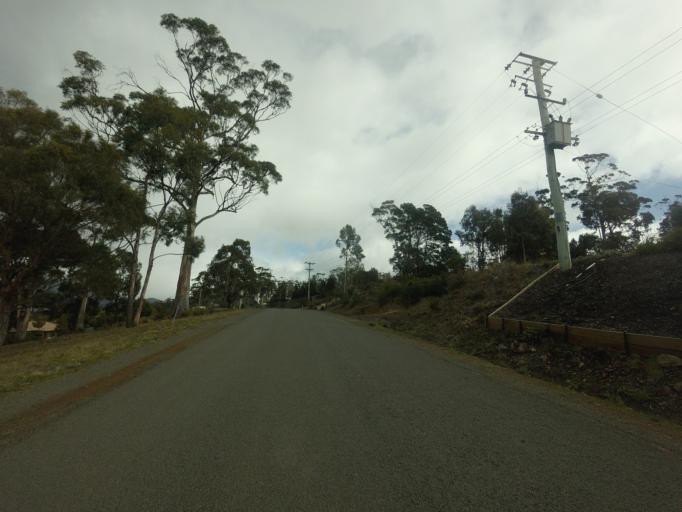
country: AU
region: Tasmania
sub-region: Sorell
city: Sorell
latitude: -42.5394
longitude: 147.9121
